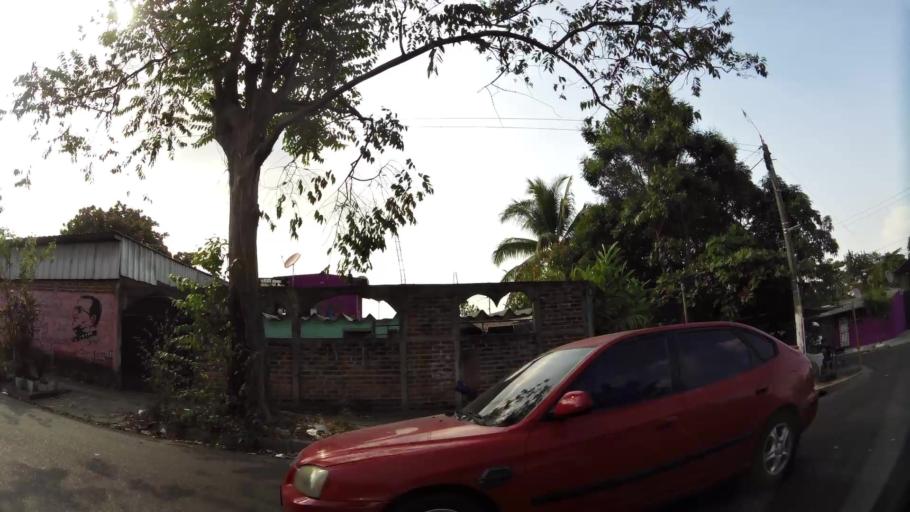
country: SV
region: San Salvador
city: Soyapango
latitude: 13.7242
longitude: -89.1271
